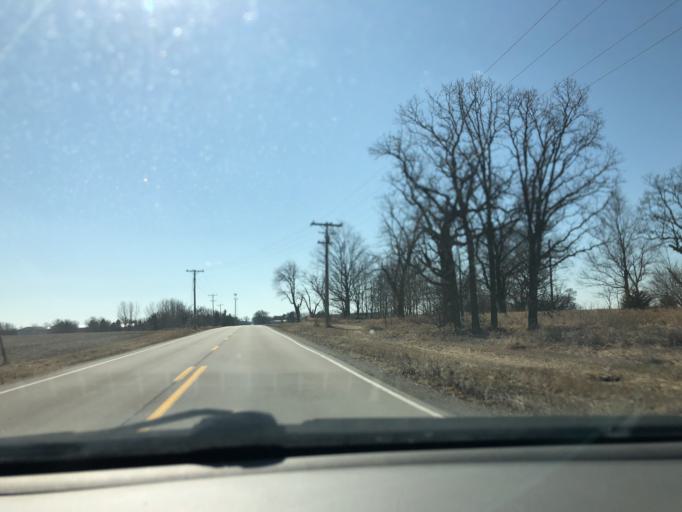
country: US
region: Illinois
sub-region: Kane County
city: Hampshire
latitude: 42.1296
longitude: -88.5350
